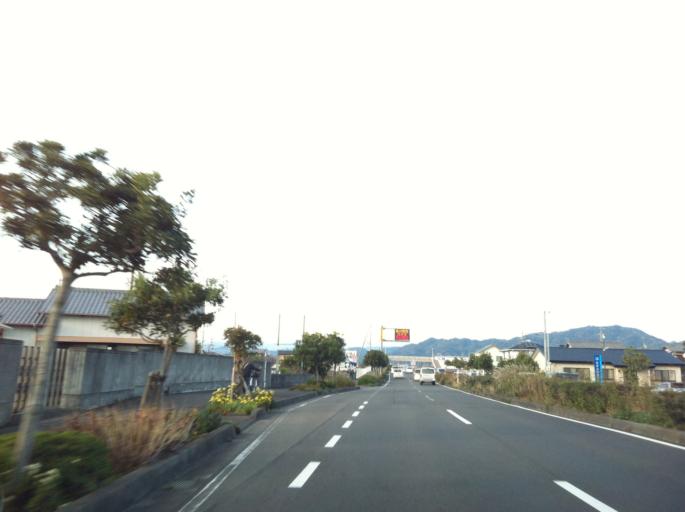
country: JP
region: Shizuoka
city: Yaizu
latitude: 34.8479
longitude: 138.2996
